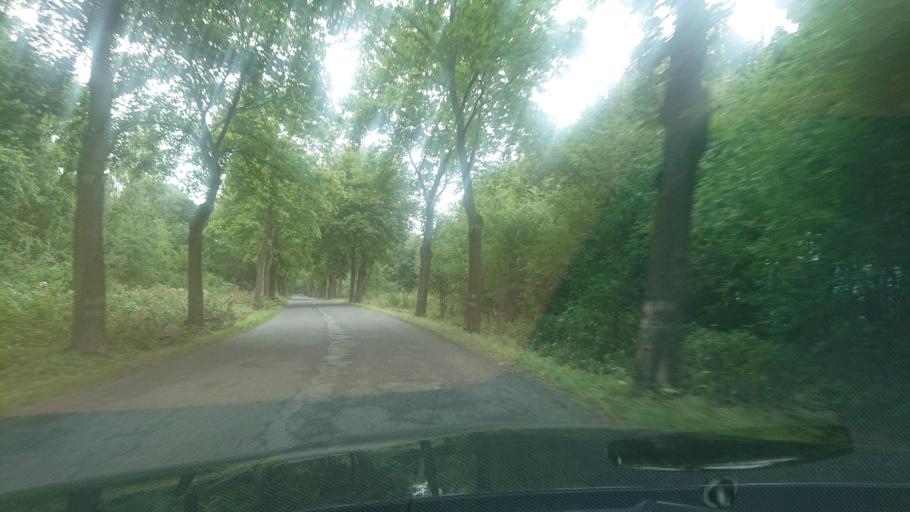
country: PL
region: Lower Silesian Voivodeship
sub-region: Powiat klodzki
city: Miedzylesie
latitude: 50.2215
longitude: 16.7135
